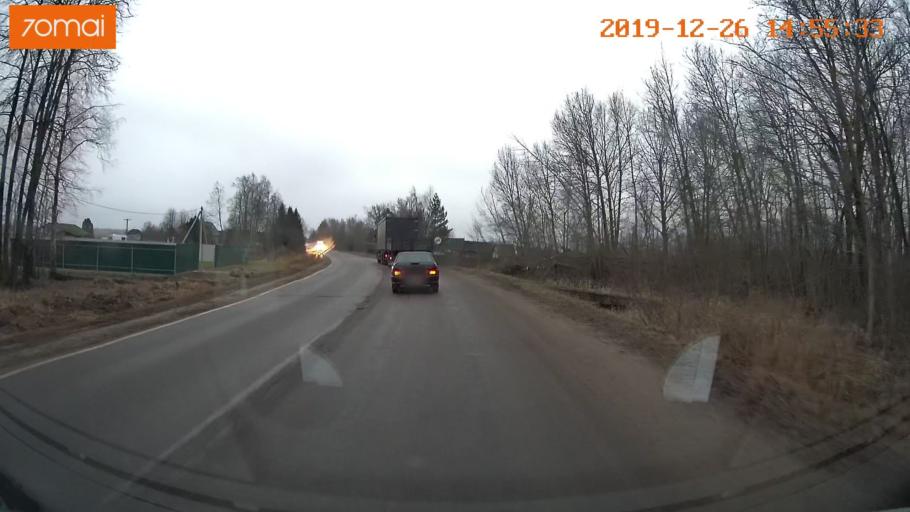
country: RU
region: Jaroslavl
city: Rybinsk
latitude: 58.3002
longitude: 38.8749
